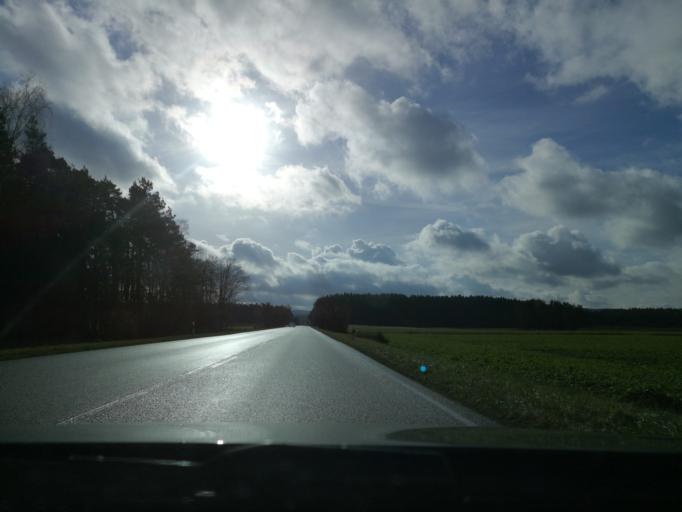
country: DE
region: Bavaria
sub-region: Regierungsbezirk Mittelfranken
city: Spalt
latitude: 49.2315
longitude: 10.8931
